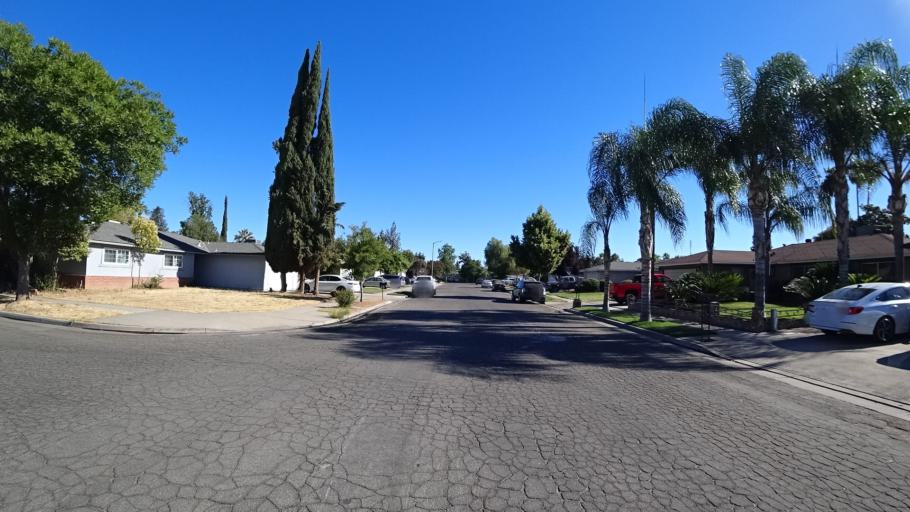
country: US
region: California
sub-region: Fresno County
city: Fresno
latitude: 36.8018
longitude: -119.8390
